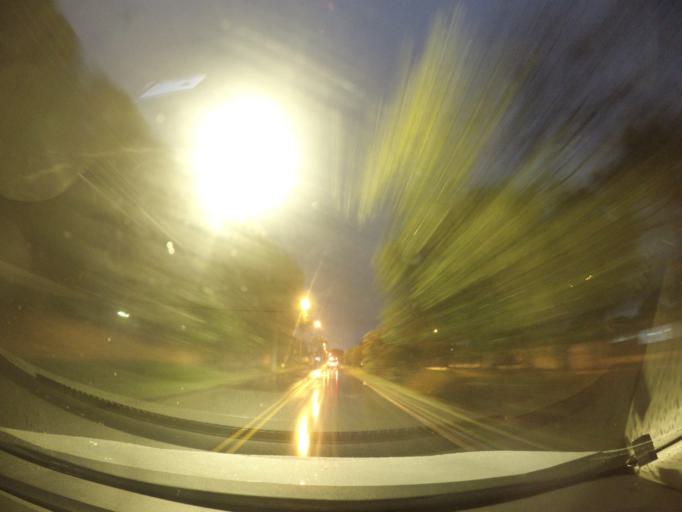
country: BR
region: Parana
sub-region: Sao Jose Dos Pinhais
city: Sao Jose dos Pinhais
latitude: -25.4973
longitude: -49.2443
